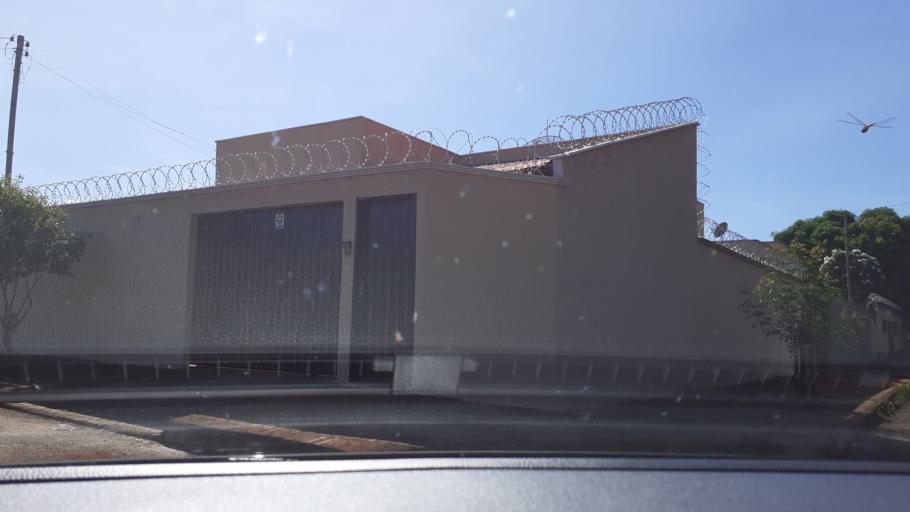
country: BR
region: Goias
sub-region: Itumbiara
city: Itumbiara
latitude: -18.4067
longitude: -49.2525
